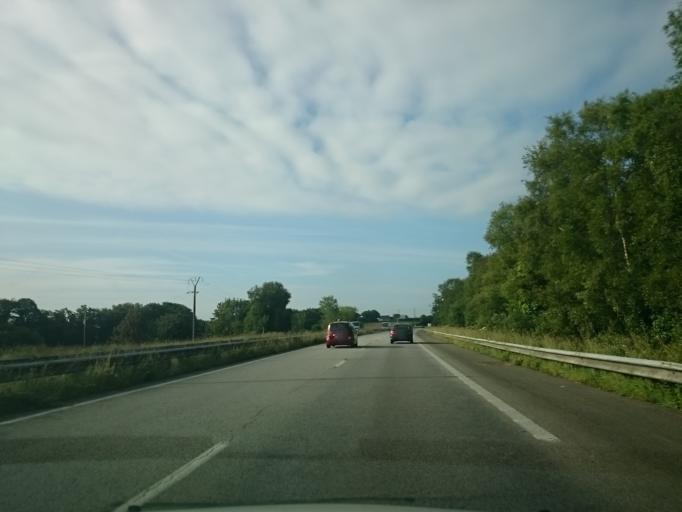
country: FR
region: Brittany
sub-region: Departement du Finistere
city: Briec
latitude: 48.1233
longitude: -4.0225
